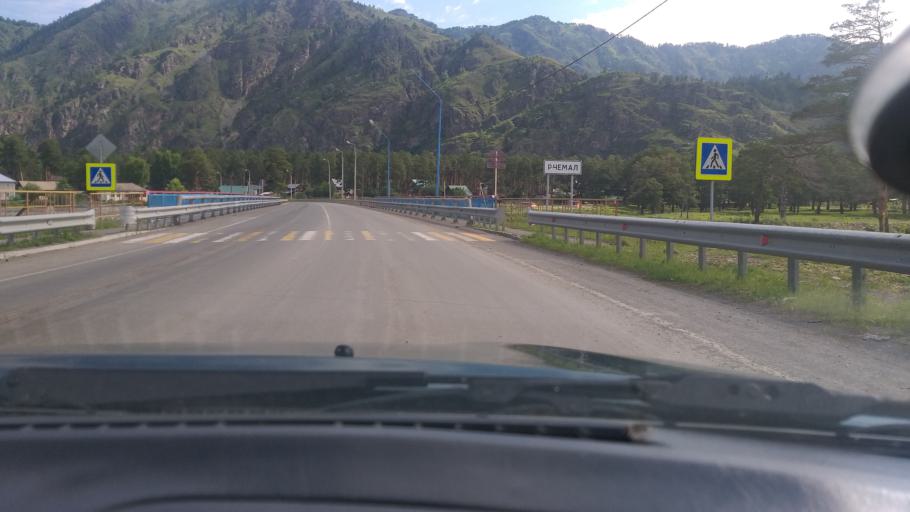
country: RU
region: Altay
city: Chemal
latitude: 51.3914
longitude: 86.0201
